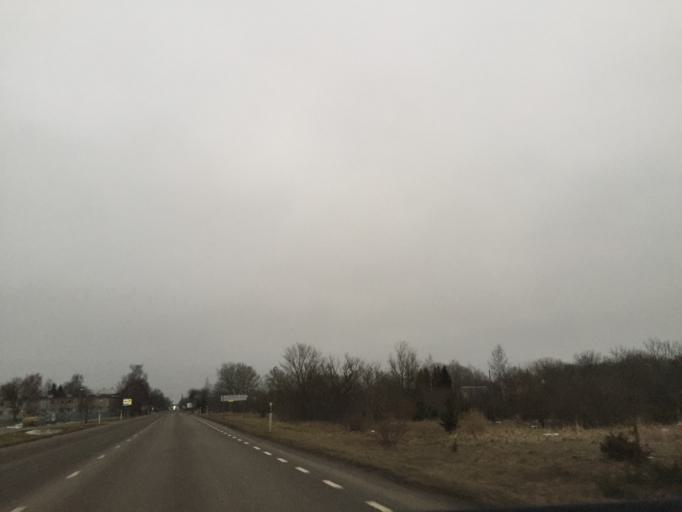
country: EE
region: Saare
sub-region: Kuressaare linn
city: Kuressaare
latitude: 58.2503
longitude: 22.5077
